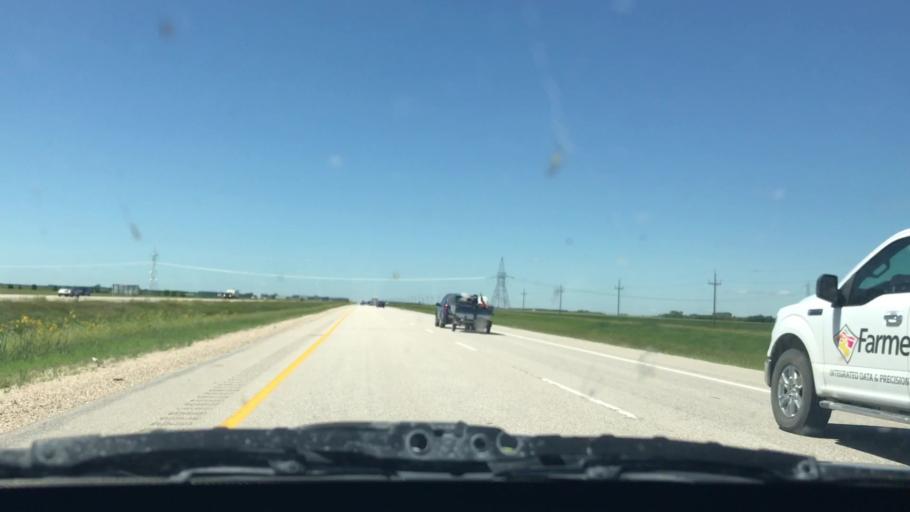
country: CA
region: Manitoba
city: Steinbach
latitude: 49.7092
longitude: -96.6660
